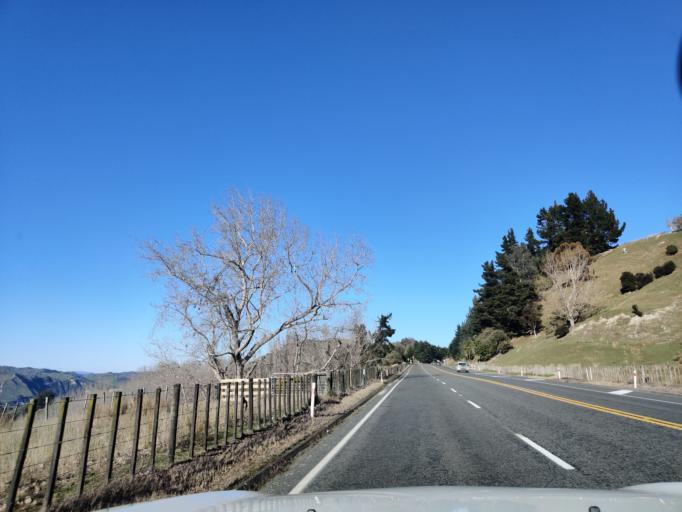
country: NZ
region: Manawatu-Wanganui
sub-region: Ruapehu District
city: Waiouru
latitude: -39.7653
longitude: 175.8017
